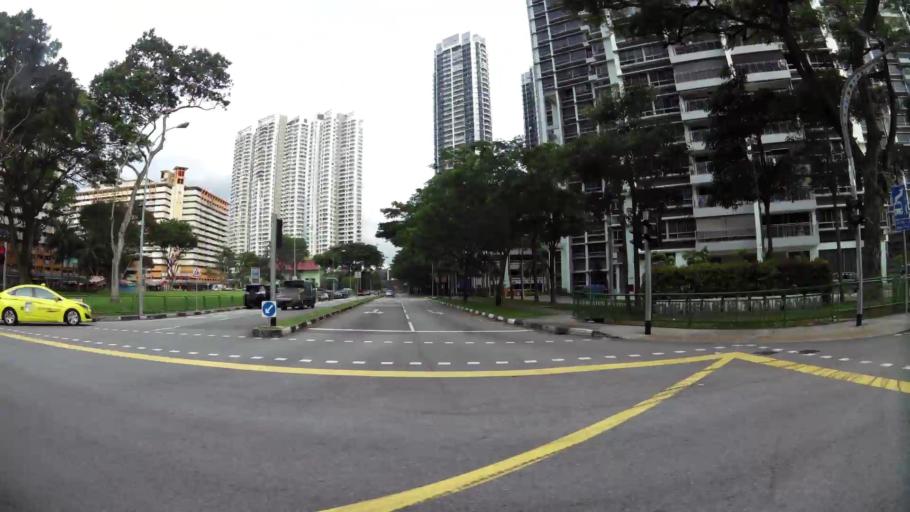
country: SG
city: Singapore
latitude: 1.3369
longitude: 103.8436
